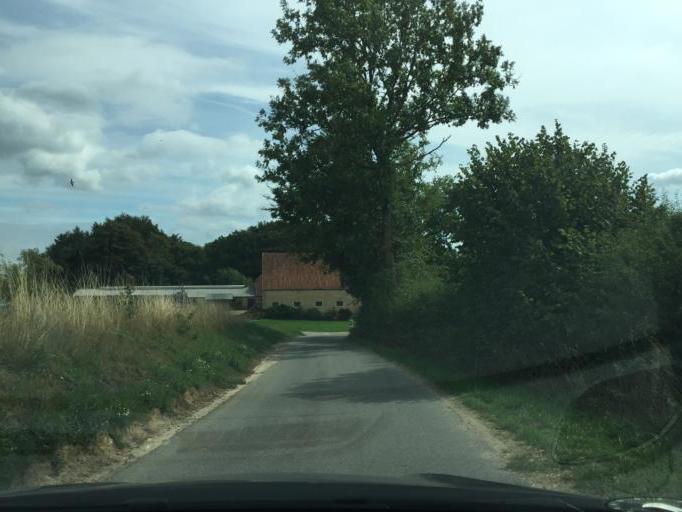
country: DK
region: South Denmark
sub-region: Assens Kommune
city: Vissenbjerg
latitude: 55.4111
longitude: 10.1953
